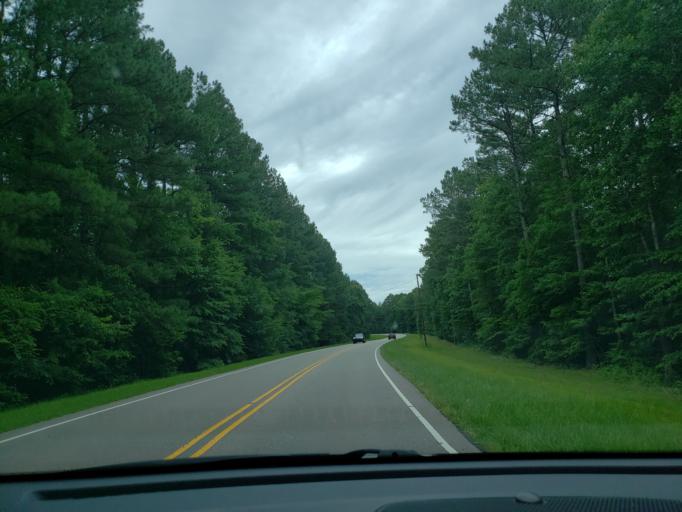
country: US
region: North Carolina
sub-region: Orange County
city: Chapel Hill
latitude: 35.8658
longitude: -79.0045
